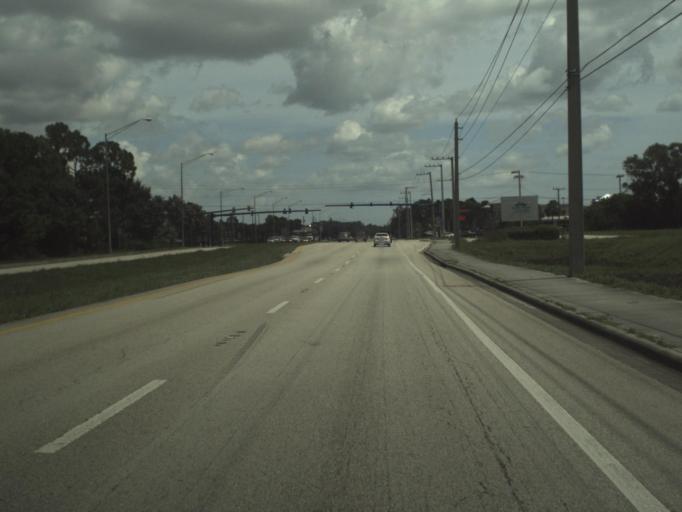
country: US
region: Florida
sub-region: Martin County
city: Palm City
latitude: 27.1222
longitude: -80.2526
